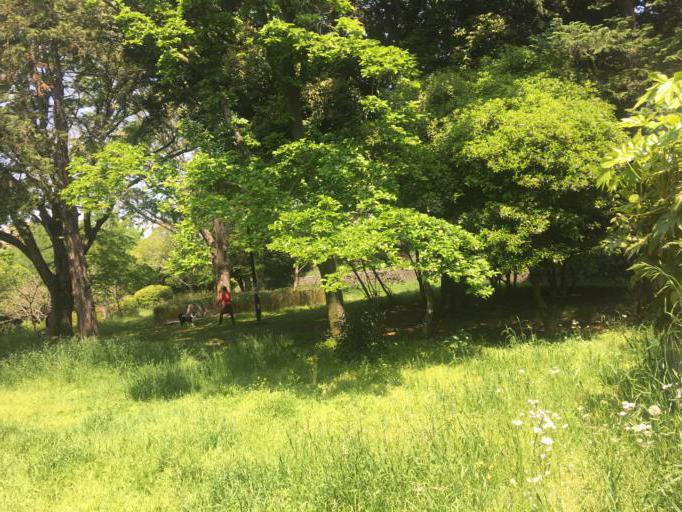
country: JP
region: Saitama
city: Wako
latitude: 35.7711
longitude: 139.6263
